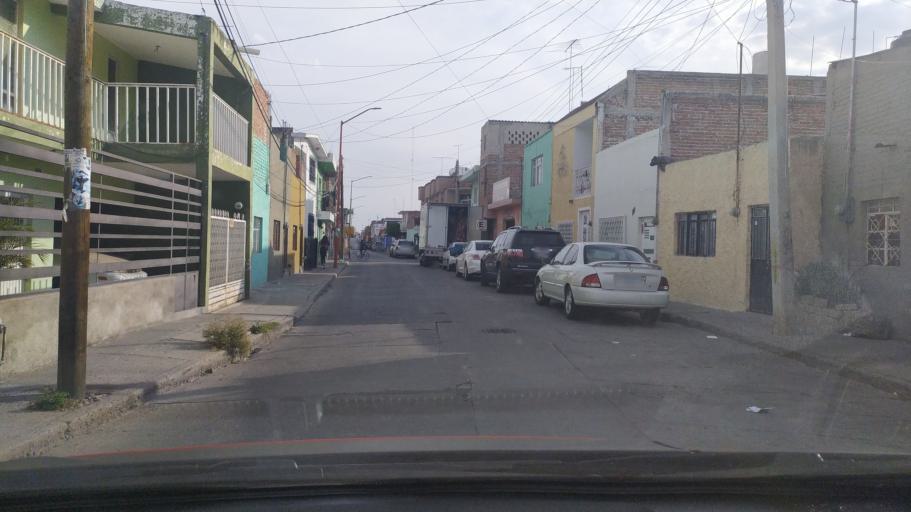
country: MX
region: Guanajuato
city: San Francisco del Rincon
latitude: 21.0250
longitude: -101.8561
